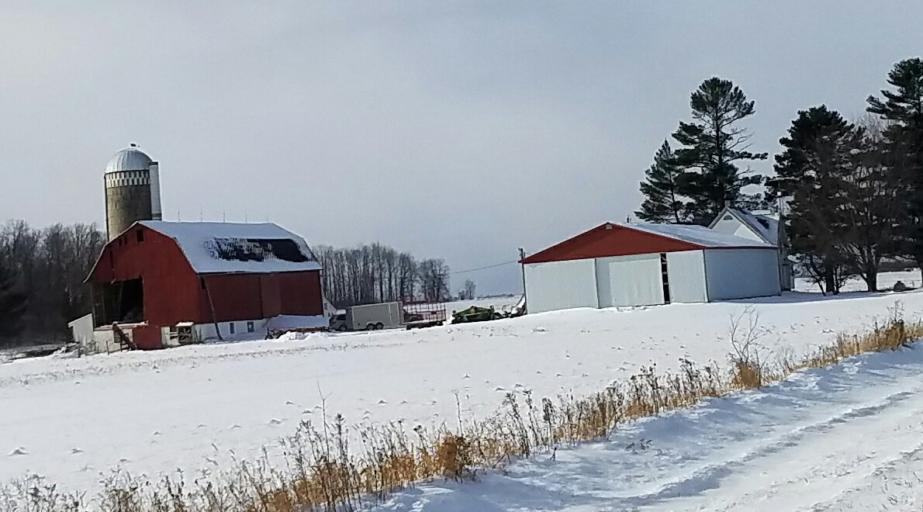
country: US
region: Wisconsin
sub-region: Clark County
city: Loyal
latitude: 44.6401
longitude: -90.4139
